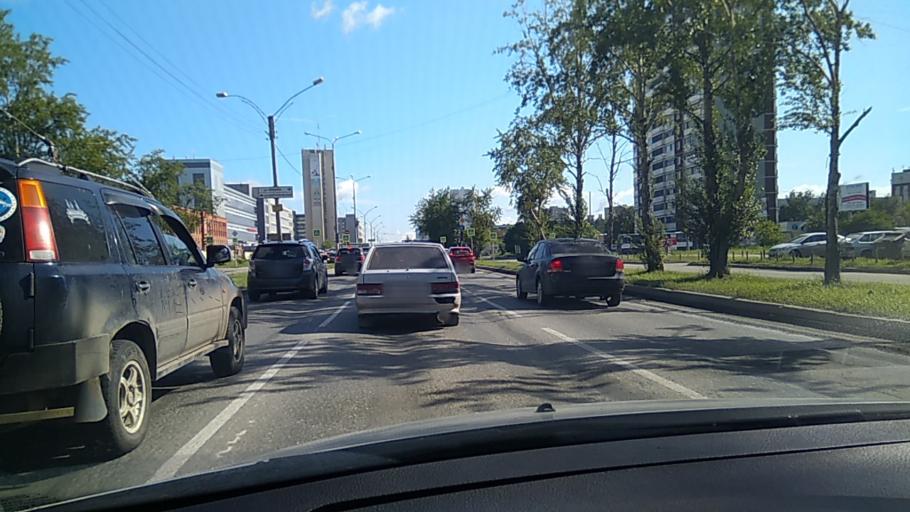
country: RU
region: Sverdlovsk
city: Sovkhoznyy
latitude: 56.8093
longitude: 60.5456
